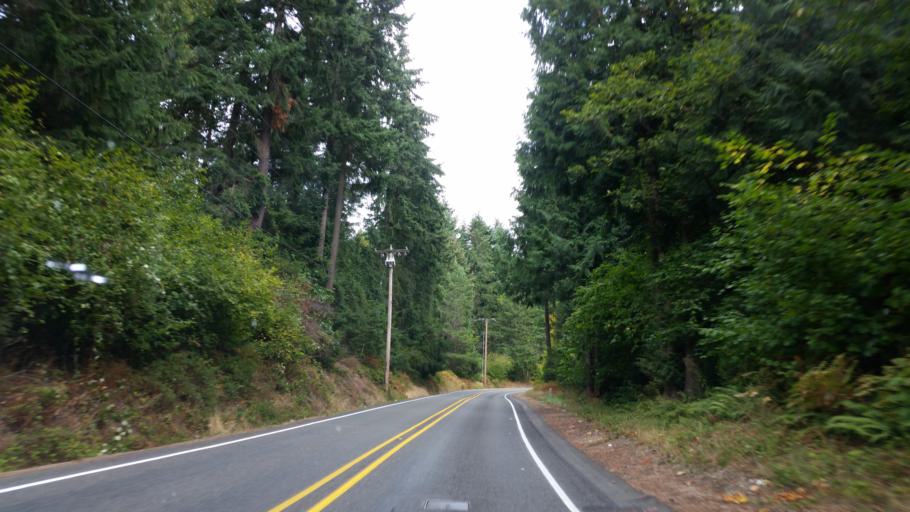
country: US
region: Washington
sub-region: Pierce County
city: Sumner
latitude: 47.2314
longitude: -122.2070
